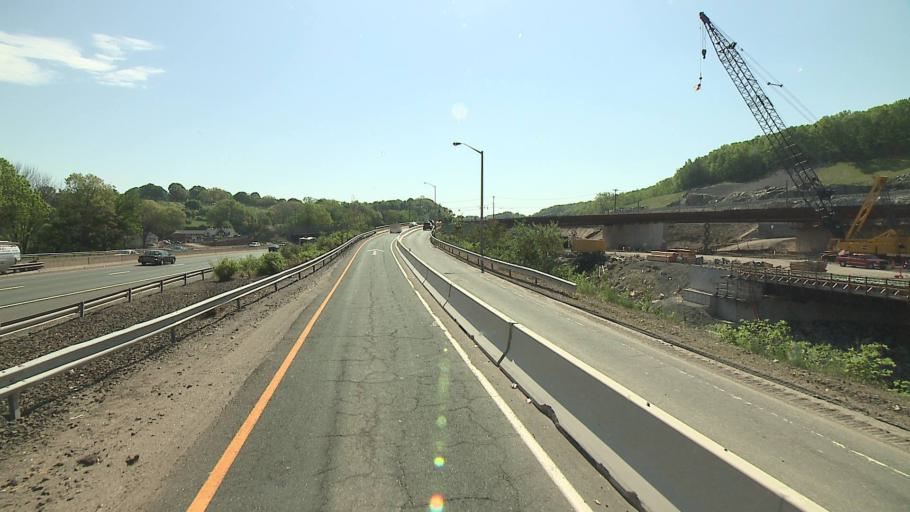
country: US
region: Connecticut
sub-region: New Haven County
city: Waterbury
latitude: 41.5397
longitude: -73.0116
